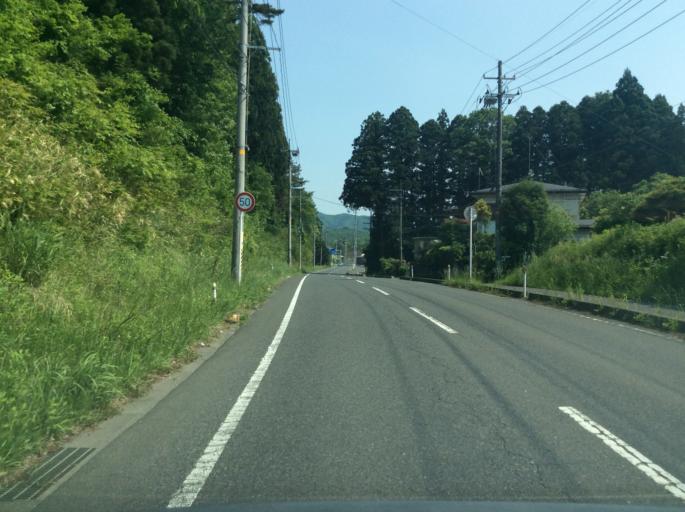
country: JP
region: Fukushima
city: Ishikawa
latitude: 37.1089
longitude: 140.2281
